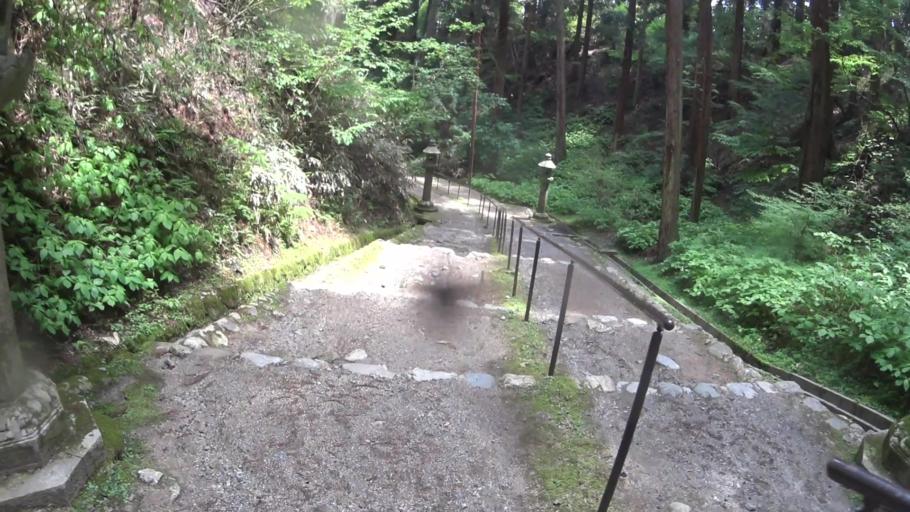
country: JP
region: Shiga Prefecture
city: Otsu-shi
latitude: 35.0702
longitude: 135.8343
